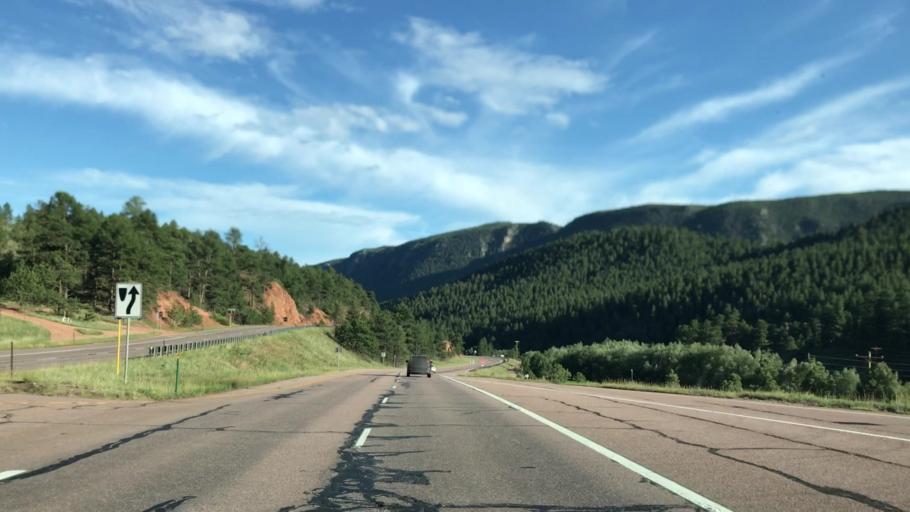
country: US
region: Colorado
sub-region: El Paso County
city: Cascade-Chipita Park
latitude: 38.9542
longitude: -105.0268
